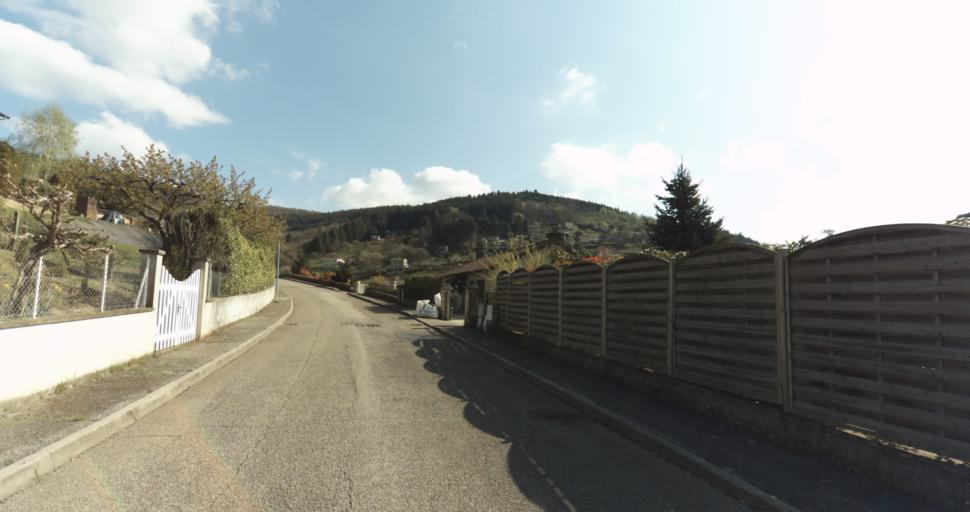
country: FR
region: Rhone-Alpes
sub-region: Departement du Rhone
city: Tarare
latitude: 45.8921
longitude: 4.4498
